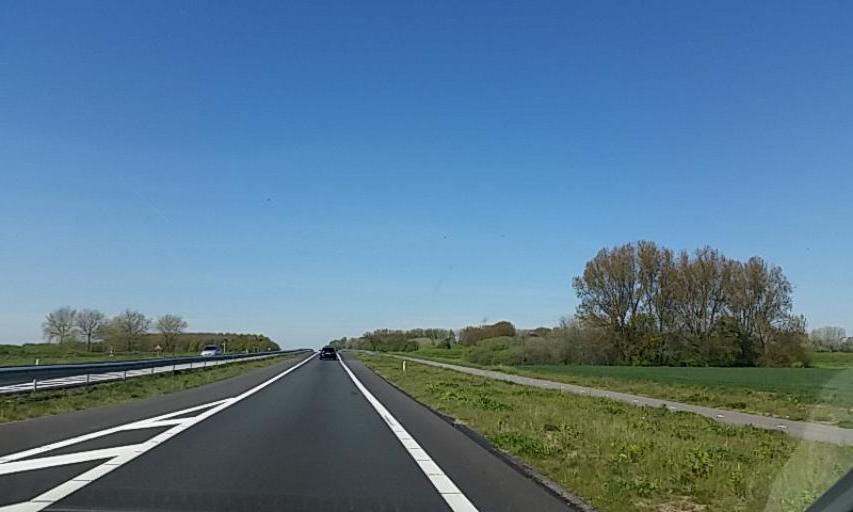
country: BE
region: Flanders
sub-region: Provincie Oost-Vlaanderen
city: Assenede
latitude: 51.3125
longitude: 3.7389
